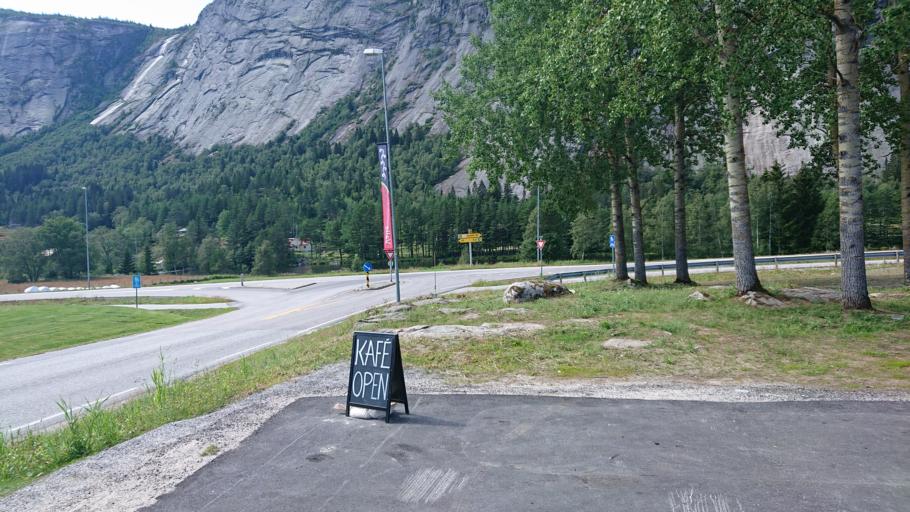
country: NO
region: Aust-Agder
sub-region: Valle
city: Valle
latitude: 59.2132
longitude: 7.5331
